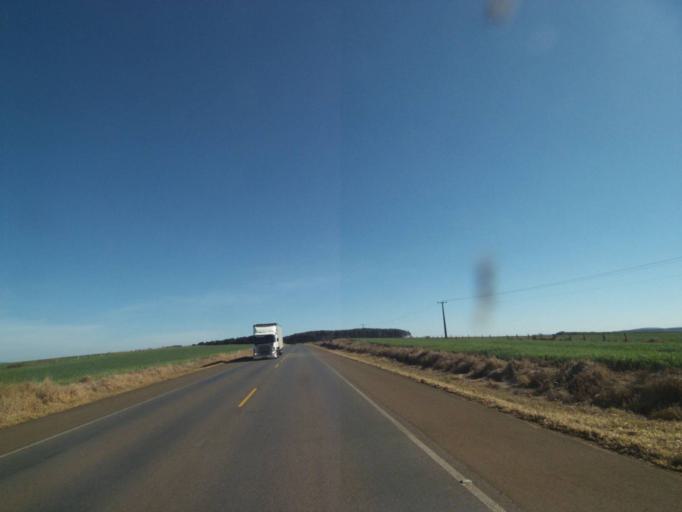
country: BR
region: Parana
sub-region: Tibagi
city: Tibagi
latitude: -24.4302
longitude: -50.4077
